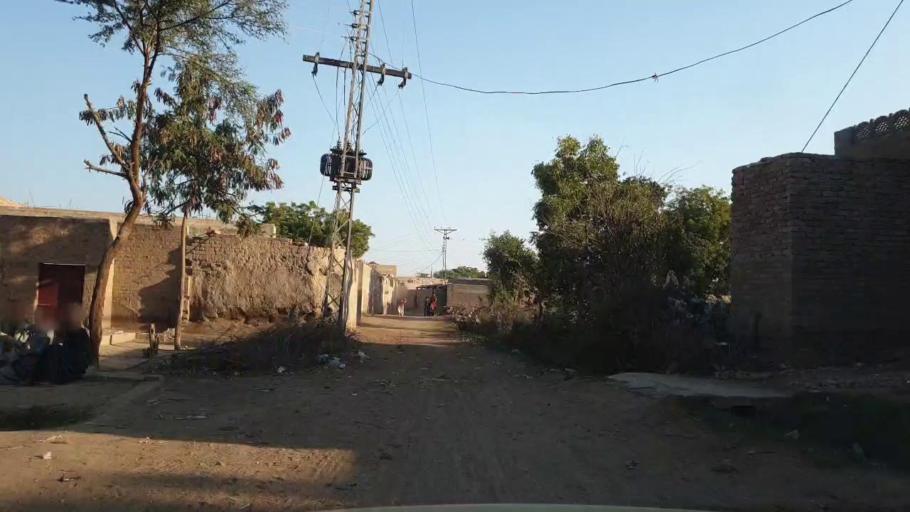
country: PK
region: Sindh
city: Tando Allahyar
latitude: 25.4965
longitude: 68.6255
